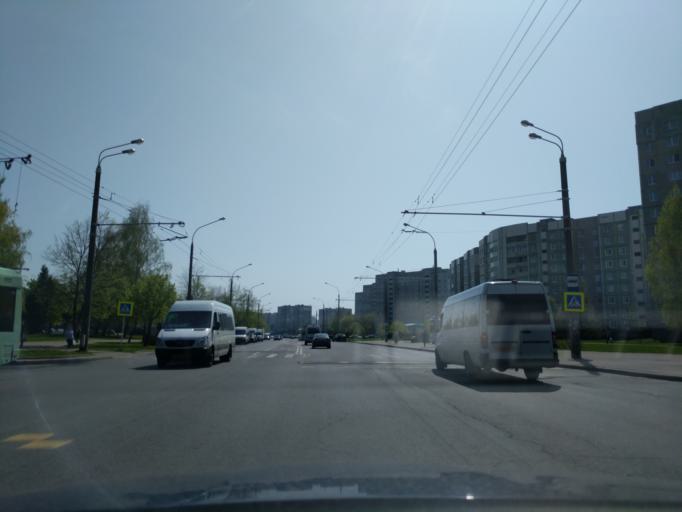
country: BY
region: Minsk
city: Malinovka
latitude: 53.8629
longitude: 27.4568
